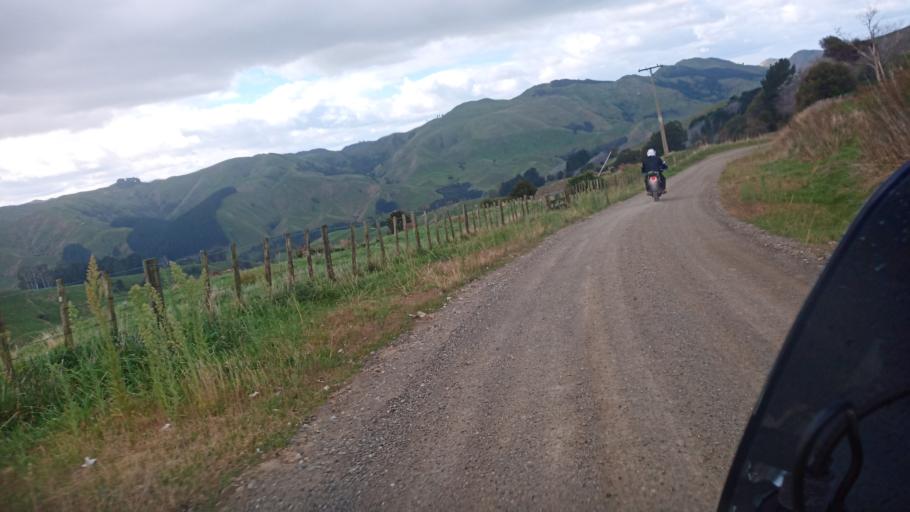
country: NZ
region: Gisborne
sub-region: Gisborne District
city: Gisborne
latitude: -38.4646
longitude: 177.6231
